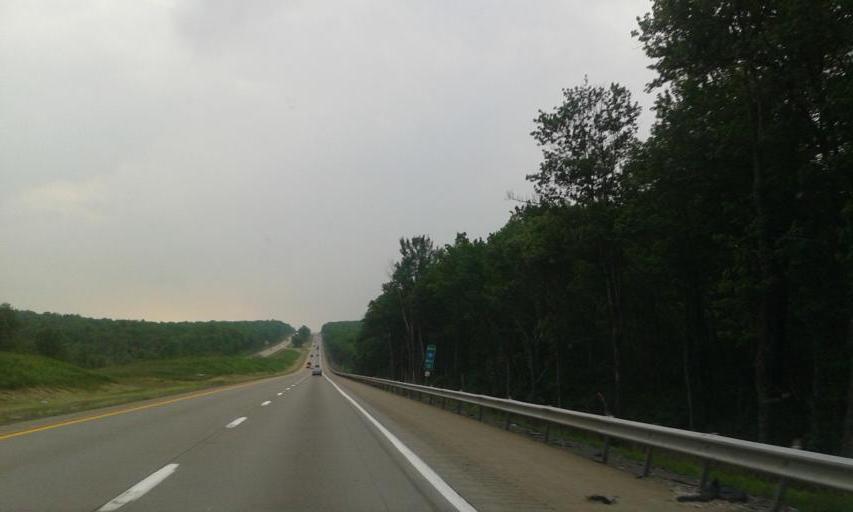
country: US
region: Pennsylvania
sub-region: Monroe County
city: Pocono Pines
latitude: 41.2000
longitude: -75.4548
